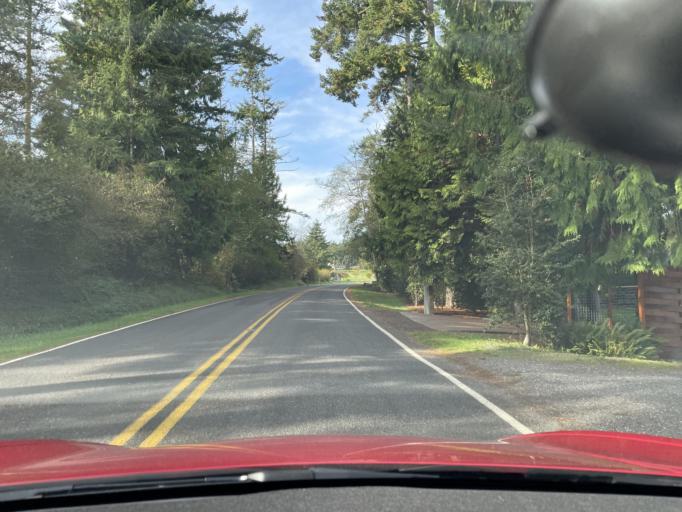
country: US
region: Washington
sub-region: San Juan County
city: Friday Harbor
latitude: 48.5261
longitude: -122.9773
